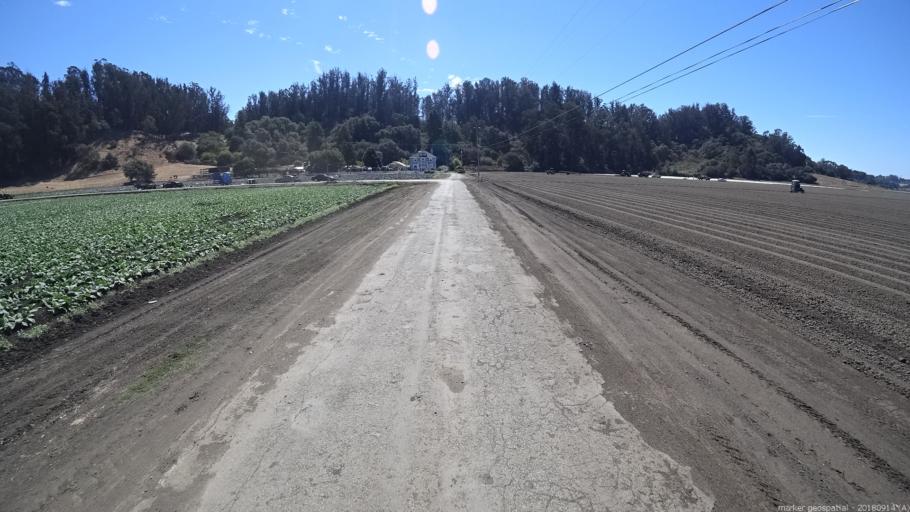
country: US
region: California
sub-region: Monterey County
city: Pajaro
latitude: 36.8918
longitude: -121.7278
